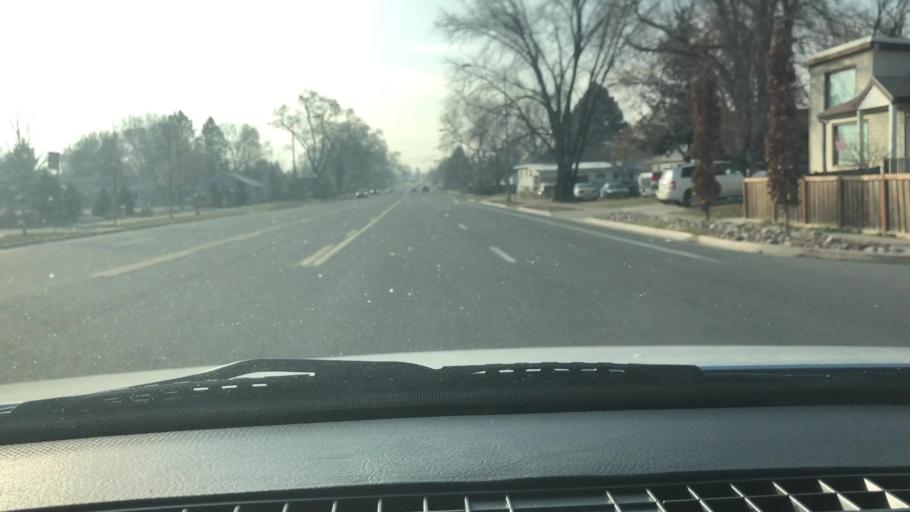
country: US
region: Utah
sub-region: Utah County
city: Provo
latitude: 40.2383
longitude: -111.6432
